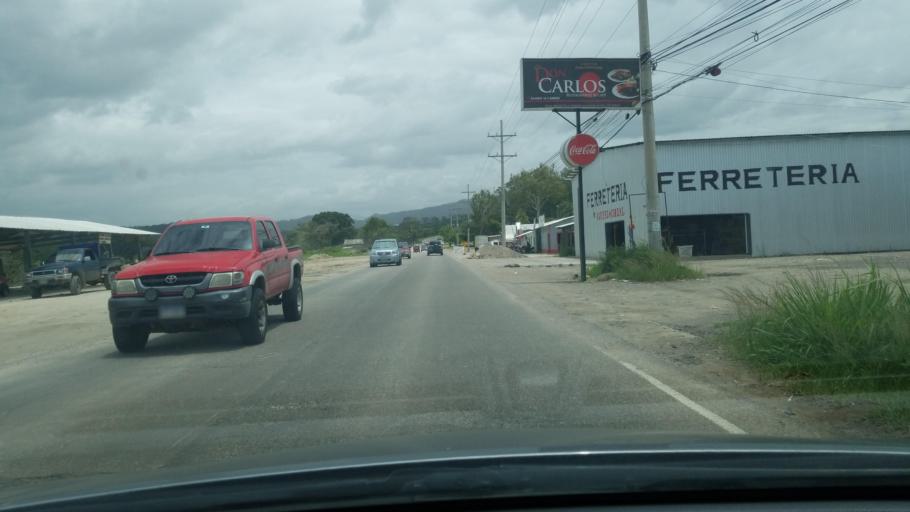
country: HN
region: Copan
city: Cucuyagua
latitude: 14.6507
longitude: -88.8776
